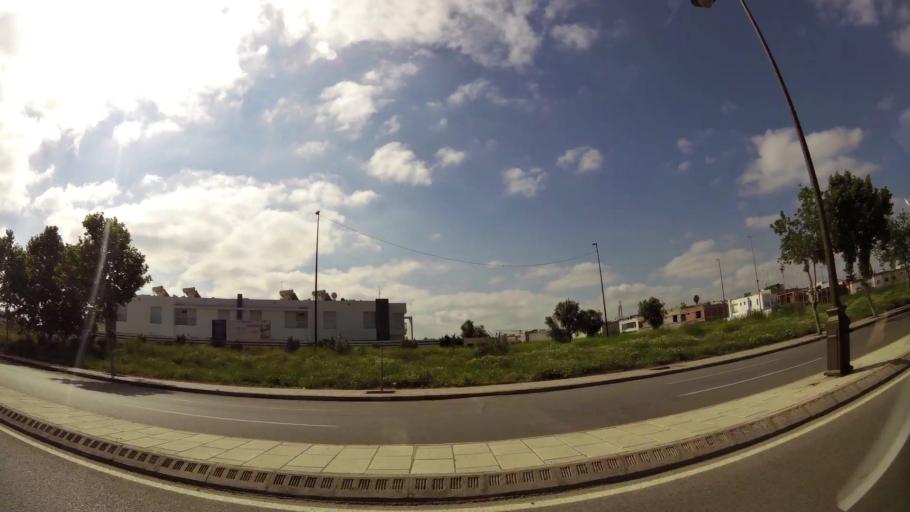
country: MA
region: Fes-Boulemane
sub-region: Fes
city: Fes
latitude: 34.0281
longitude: -5.0185
